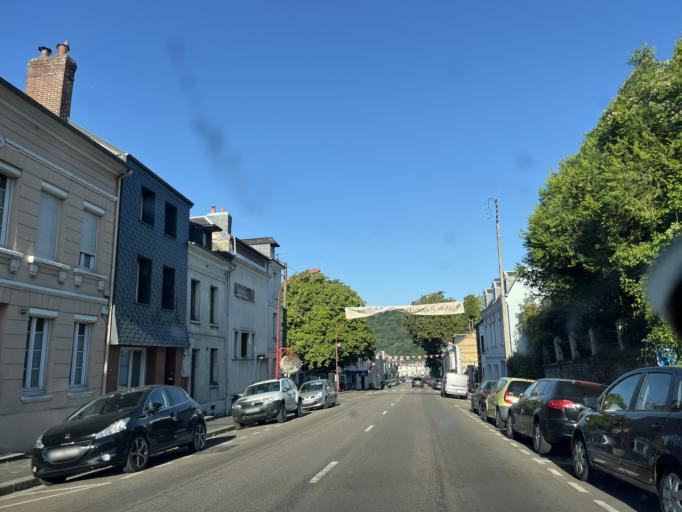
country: FR
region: Haute-Normandie
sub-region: Departement de la Seine-Maritime
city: Lillebonne
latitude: 49.5180
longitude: 0.5411
